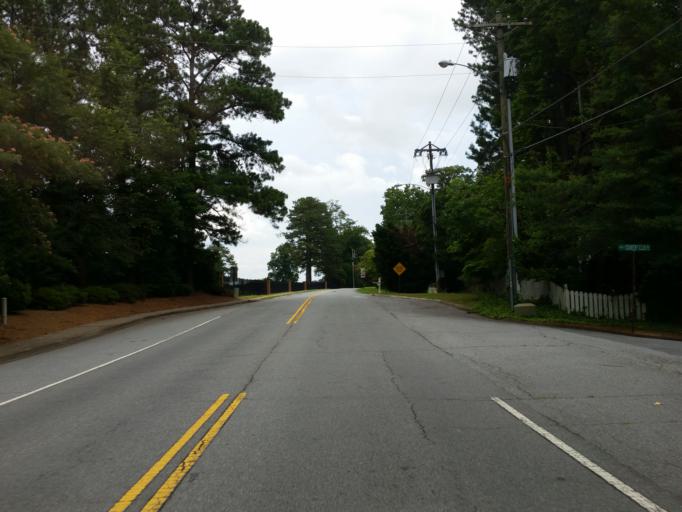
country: US
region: Georgia
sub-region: Cobb County
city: Kennesaw
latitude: 34.0394
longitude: -84.5966
